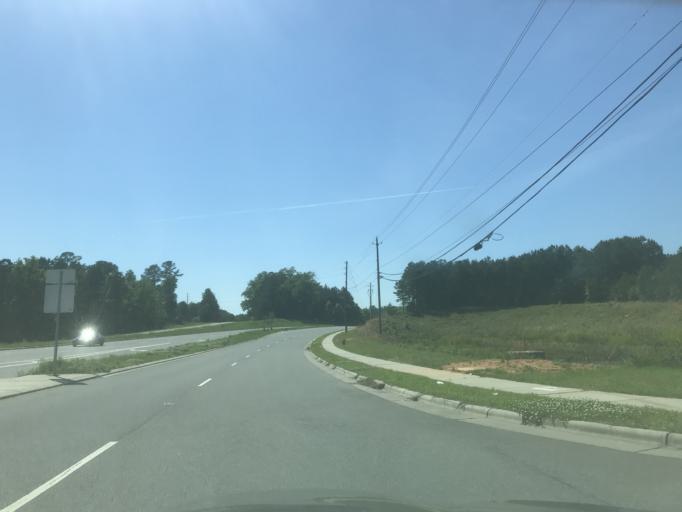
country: US
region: North Carolina
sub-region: Wake County
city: Raleigh
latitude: 35.7314
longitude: -78.6539
